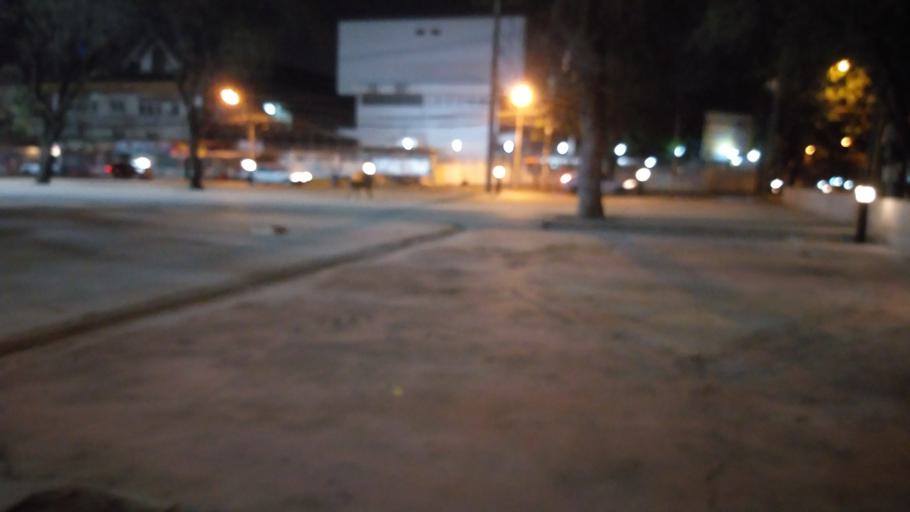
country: TH
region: Khon Kaen
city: Khon Kaen
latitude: 16.4403
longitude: 102.8353
